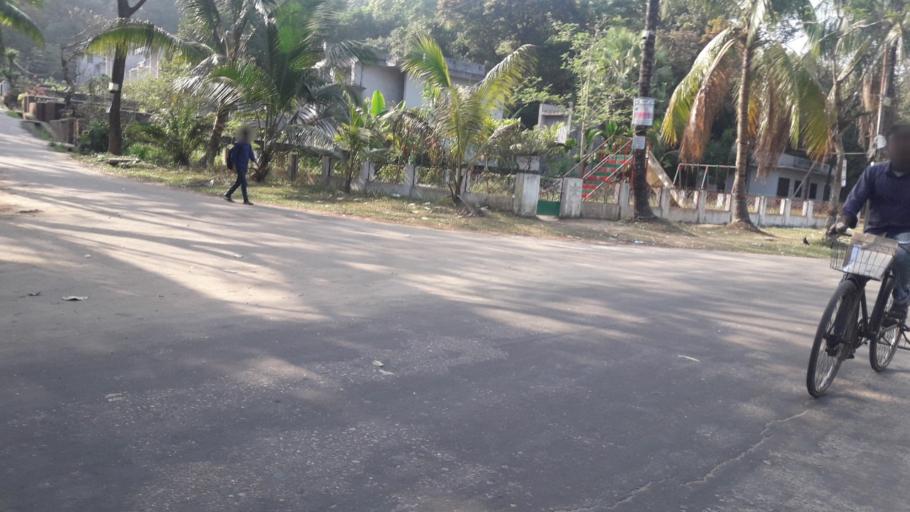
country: BD
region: Chittagong
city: Chittagong
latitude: 22.4684
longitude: 91.7940
